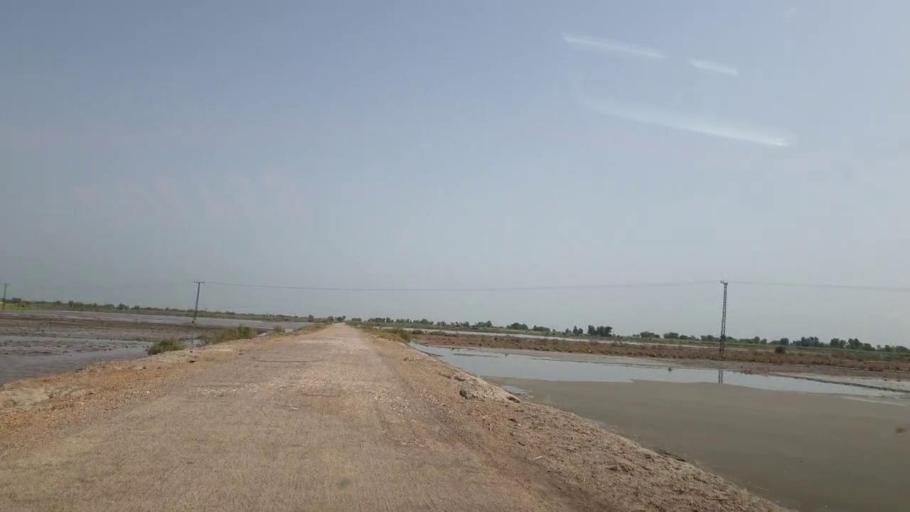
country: PK
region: Sindh
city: Sakrand
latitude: 26.2991
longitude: 68.2202
